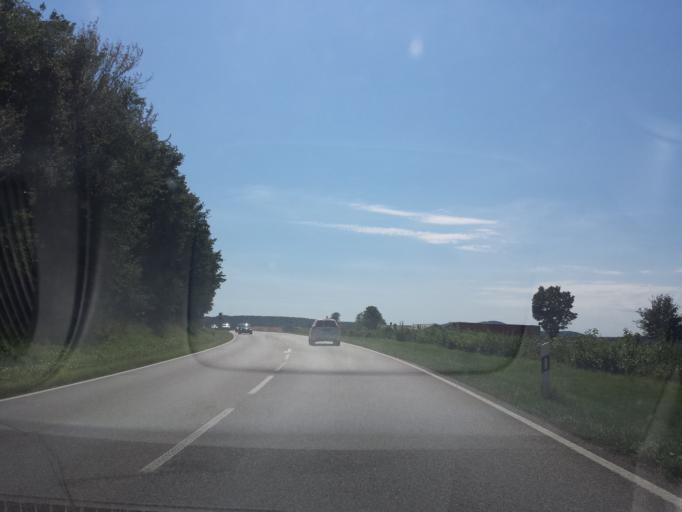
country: DE
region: Bavaria
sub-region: Upper Palatinate
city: Cham
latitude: 49.1960
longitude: 12.6559
